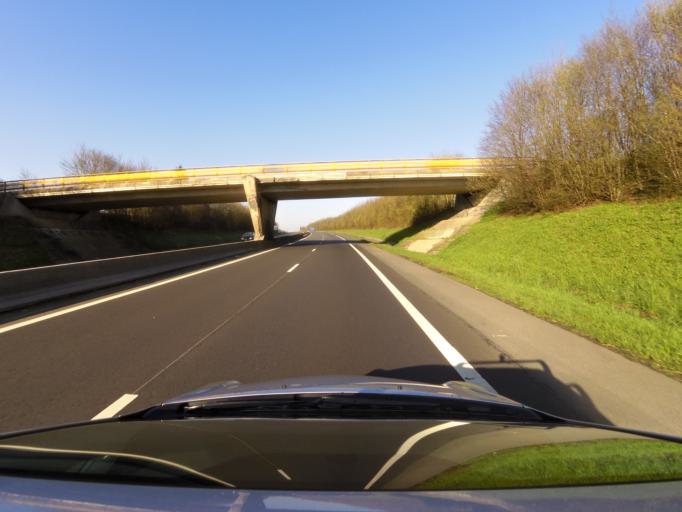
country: FR
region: Lower Normandy
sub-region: Departement du Calvados
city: Cahagnes
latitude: 49.0505
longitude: -0.7488
